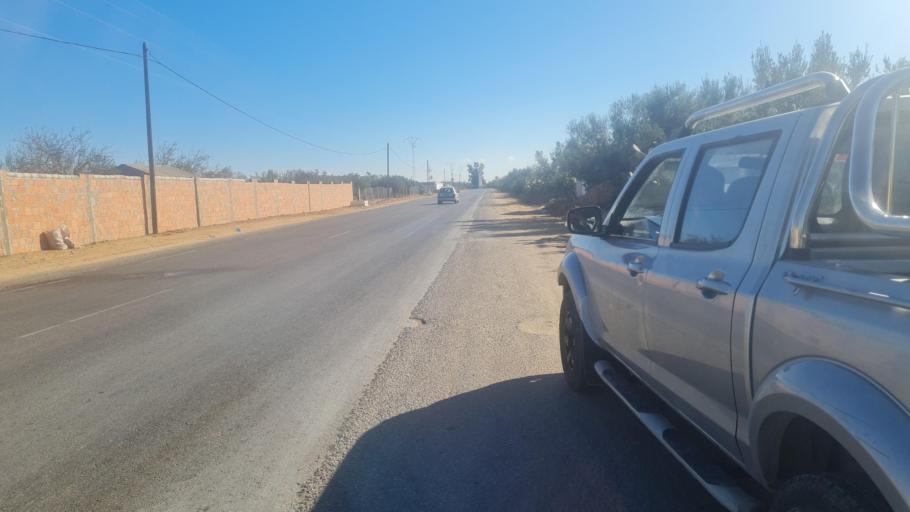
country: TN
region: Susah
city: Sidi Bou Ali
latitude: 35.9089
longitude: 10.3816
